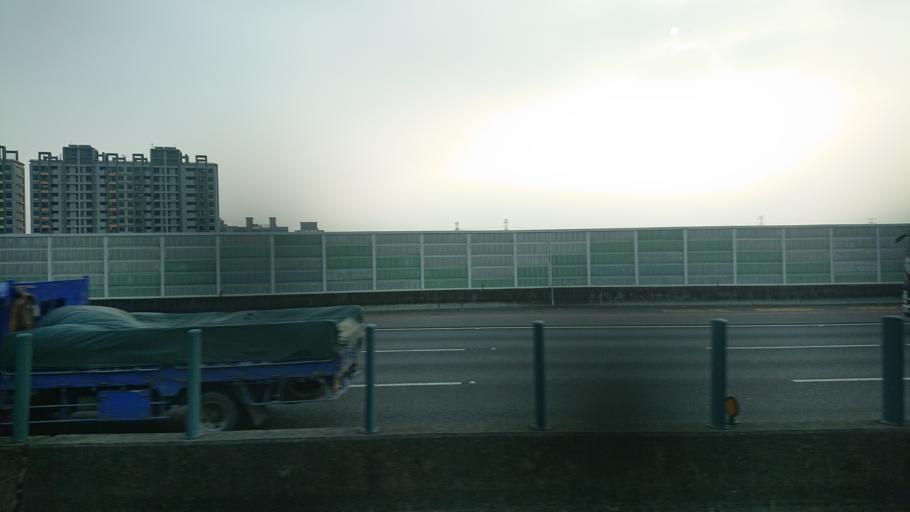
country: TW
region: Taiwan
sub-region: Changhua
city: Chang-hua
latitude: 24.1139
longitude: 120.5960
